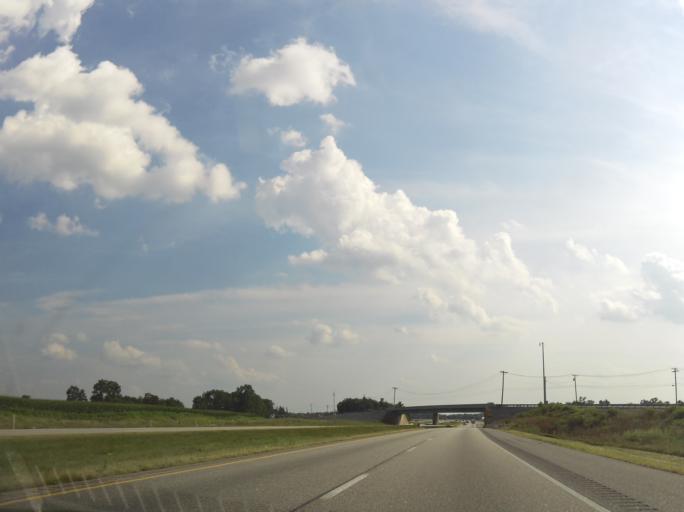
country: US
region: Pennsylvania
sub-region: Franklin County
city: Greencastle
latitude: 39.7580
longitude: -77.7260
